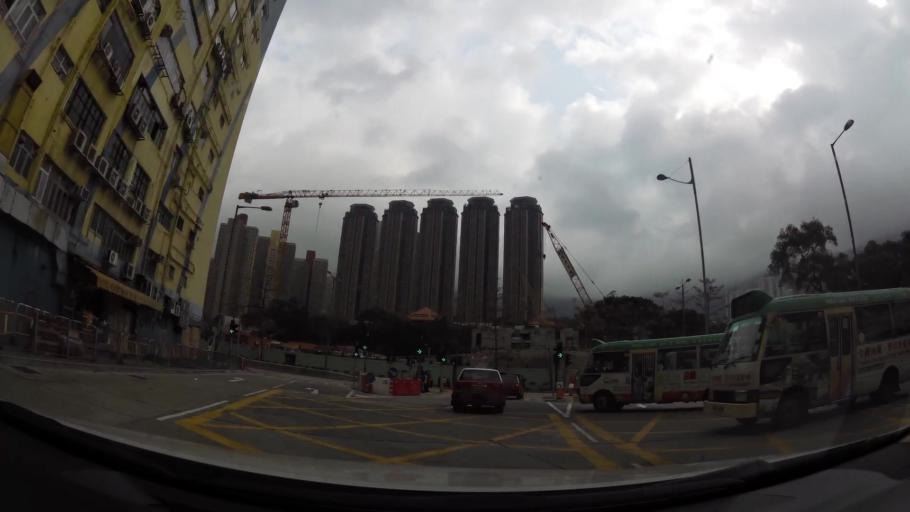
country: HK
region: Wong Tai Sin
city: Wong Tai Sin
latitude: 22.3379
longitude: 114.2012
